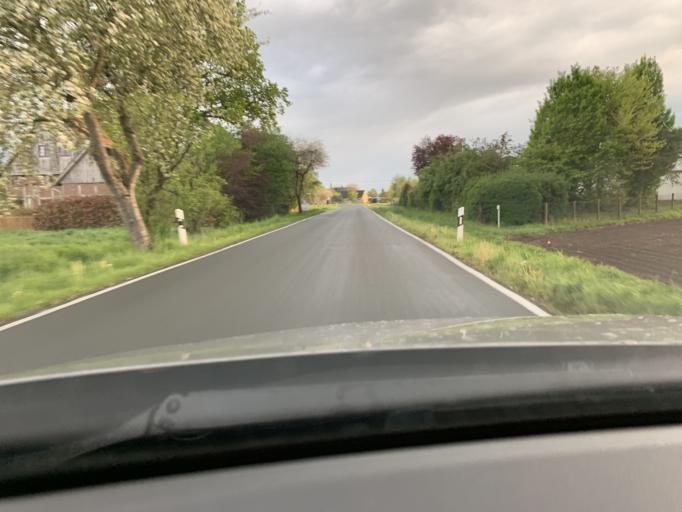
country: DE
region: North Rhine-Westphalia
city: Rietberg
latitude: 51.7779
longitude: 8.3797
